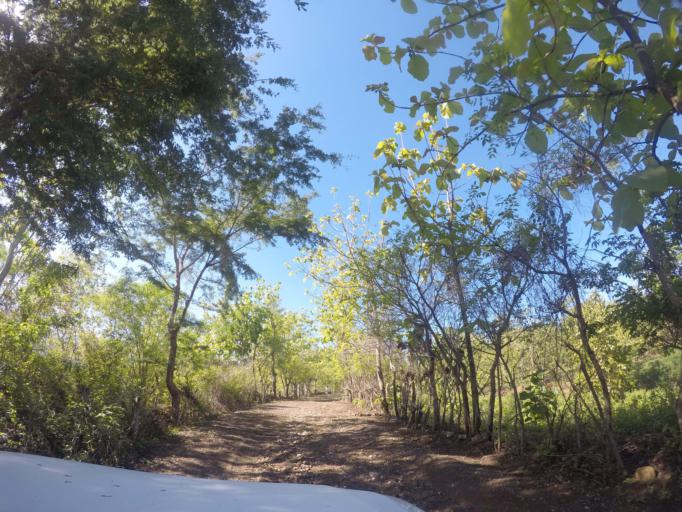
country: TL
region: Bobonaro
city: Maliana
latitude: -8.9969
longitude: 125.2051
